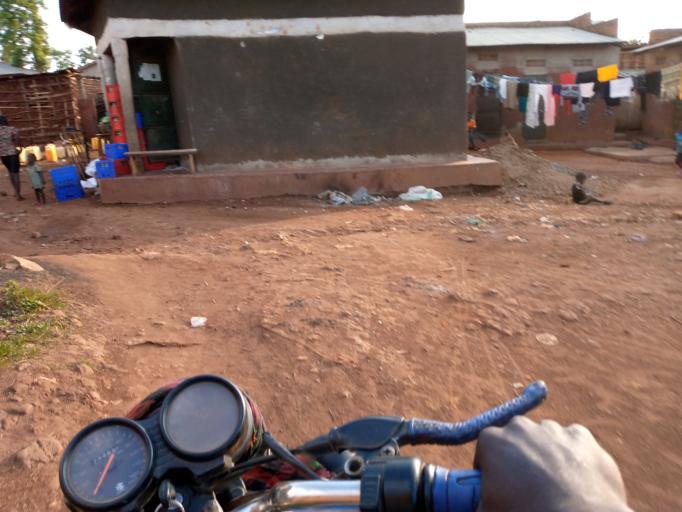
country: UG
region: Eastern Region
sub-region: Mbale District
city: Mbale
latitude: 1.0824
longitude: 34.1565
